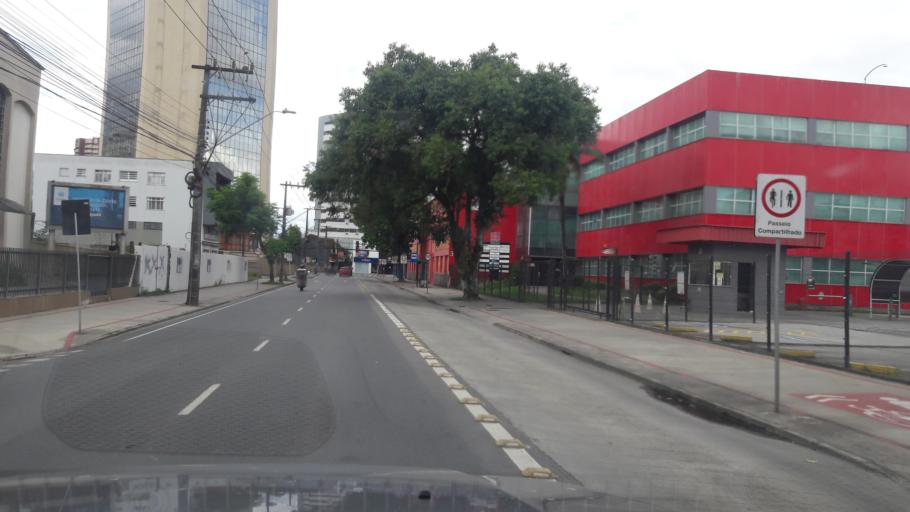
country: BR
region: Santa Catarina
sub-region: Joinville
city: Joinville
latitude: -26.3088
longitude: -48.8429
